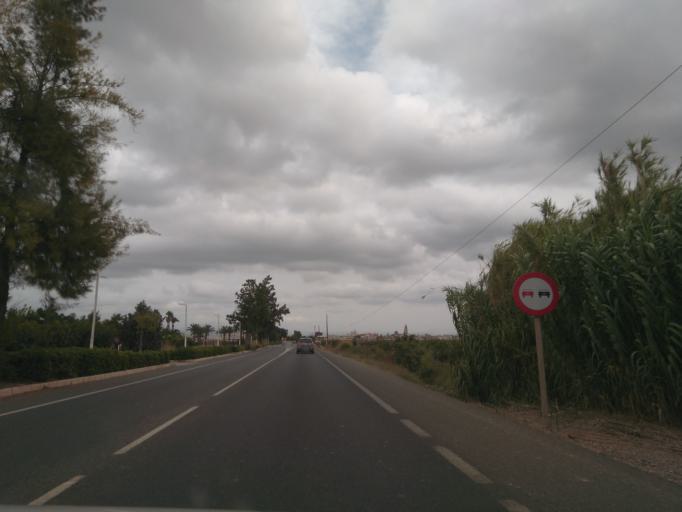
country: ES
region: Valencia
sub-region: Provincia de Valencia
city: L'Alcudia
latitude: 39.2105
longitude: -0.5118
